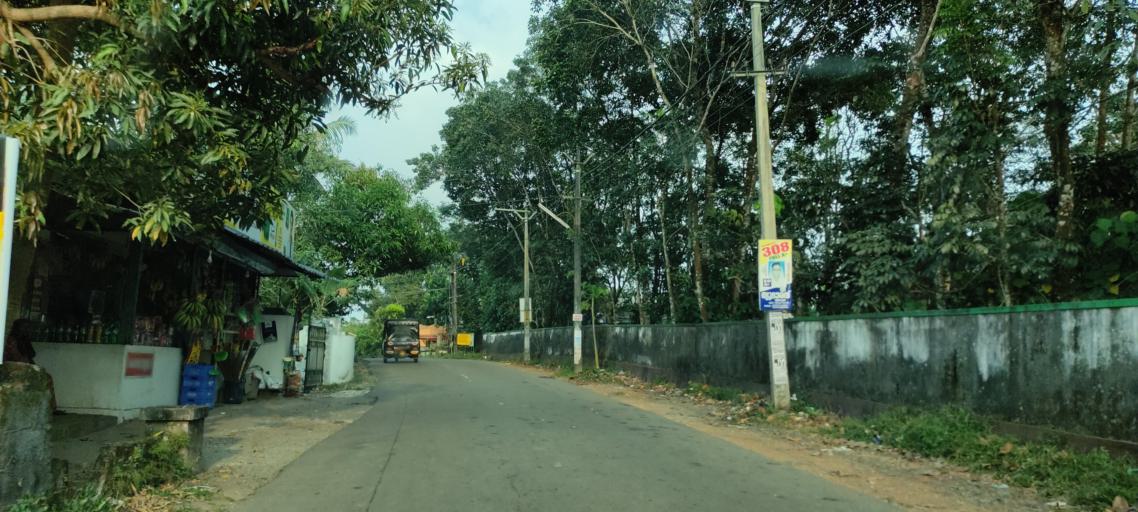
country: IN
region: Kerala
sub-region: Pattanamtitta
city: Adur
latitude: 9.0896
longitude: 76.7458
